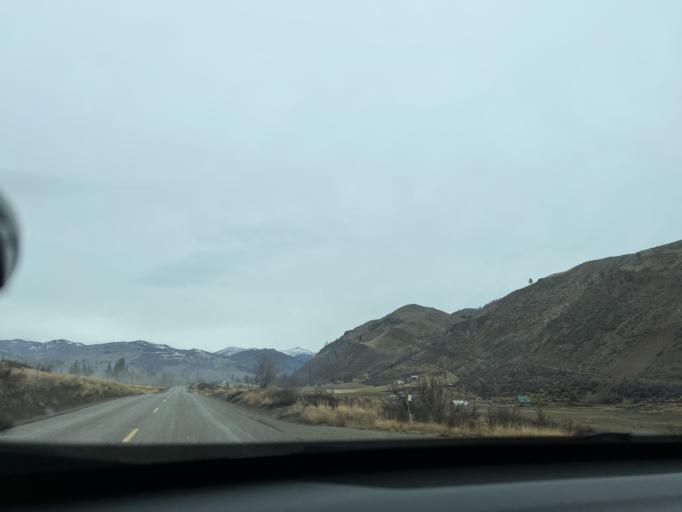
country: US
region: Washington
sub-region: Okanogan County
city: Brewster
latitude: 48.5175
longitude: -120.1764
